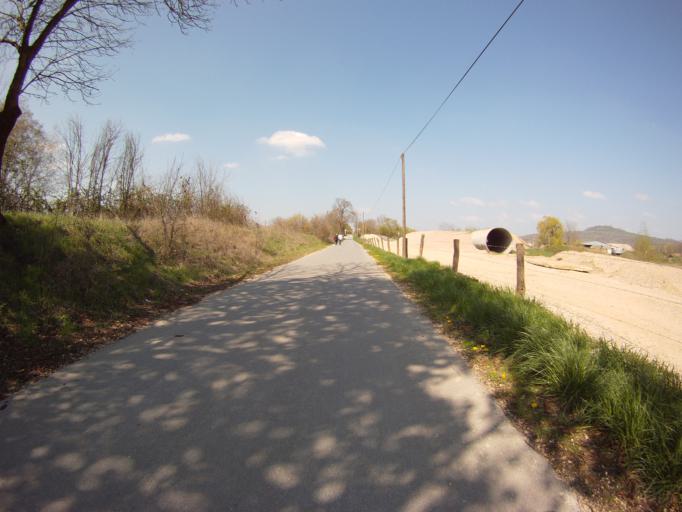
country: FR
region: Lorraine
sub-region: Departement de Meurthe-et-Moselle
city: Blenod-les-Pont-a-Mousson
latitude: 48.8823
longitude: 6.0628
